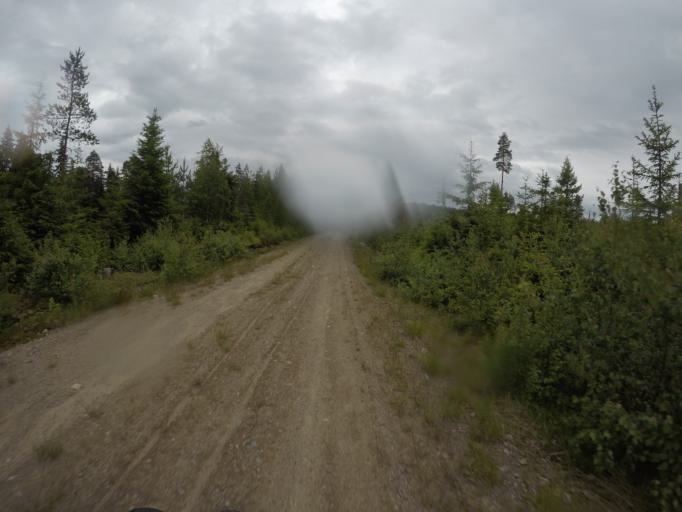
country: SE
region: Dalarna
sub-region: Ludvika Kommun
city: Abborrberget
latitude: 60.0513
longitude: 14.5791
